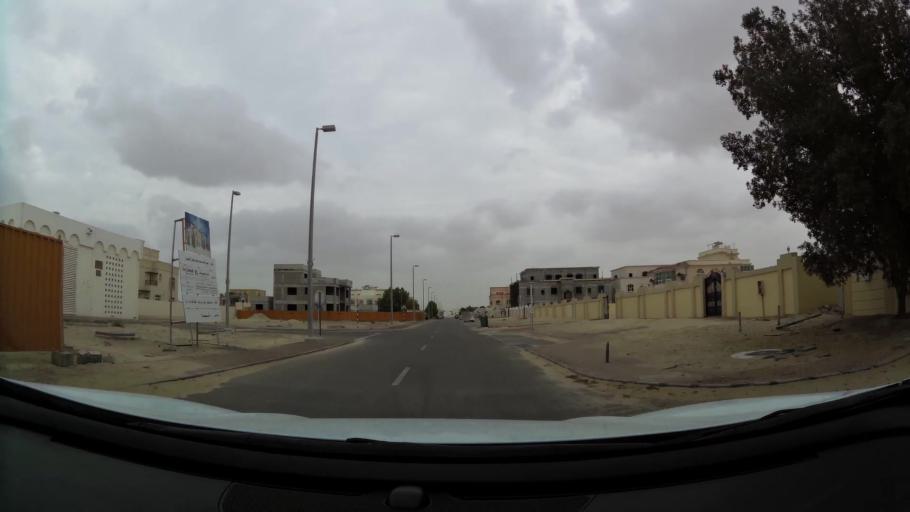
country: AE
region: Abu Dhabi
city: Abu Dhabi
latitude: 24.3768
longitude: 54.6508
